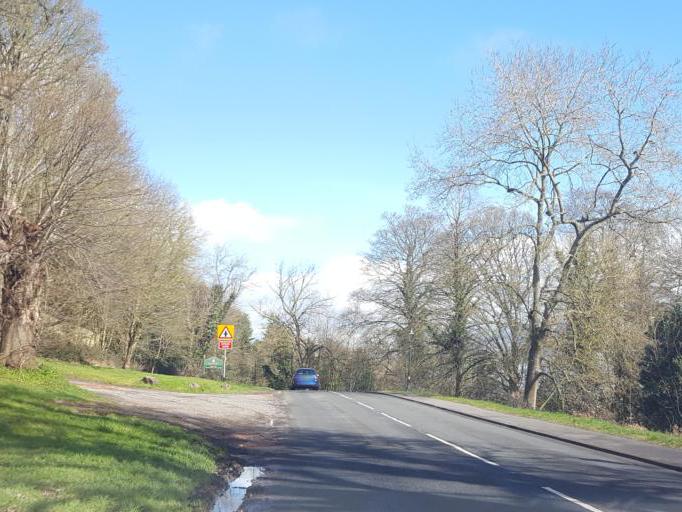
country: GB
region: England
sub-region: Worcestershire
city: Great Malvern
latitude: 52.1009
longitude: -2.3301
